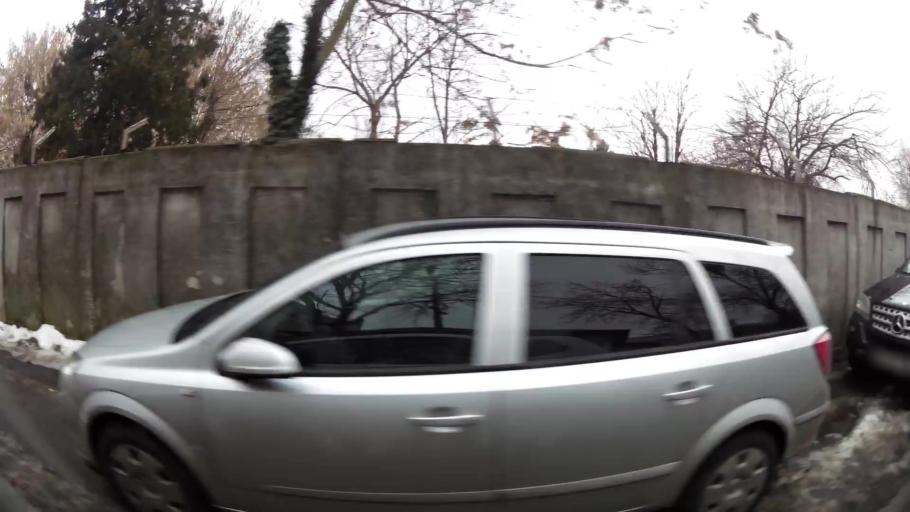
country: RO
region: Bucuresti
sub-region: Municipiul Bucuresti
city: Bucuresti
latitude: 44.4591
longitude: 26.0638
